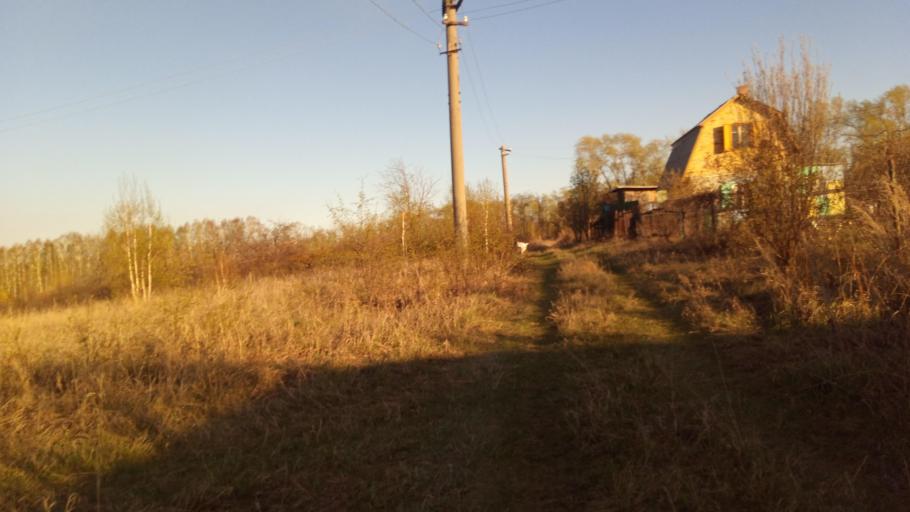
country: RU
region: Chelyabinsk
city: Timiryazevskiy
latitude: 54.9901
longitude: 60.8551
